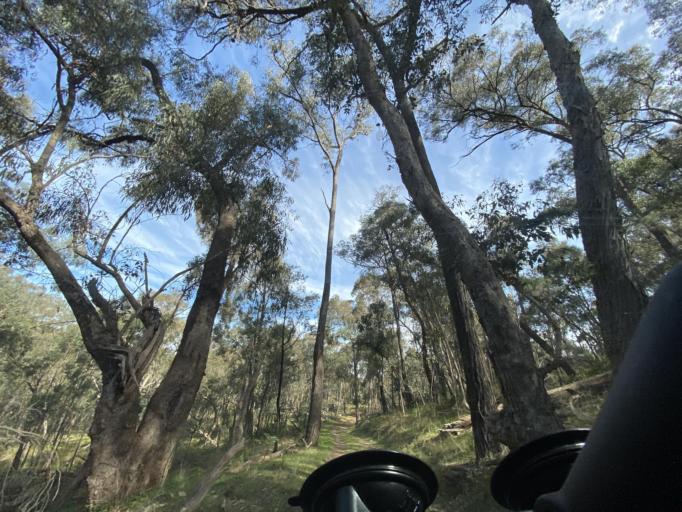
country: AU
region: Victoria
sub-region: Mansfield
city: Mansfield
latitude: -36.8105
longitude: 146.1161
